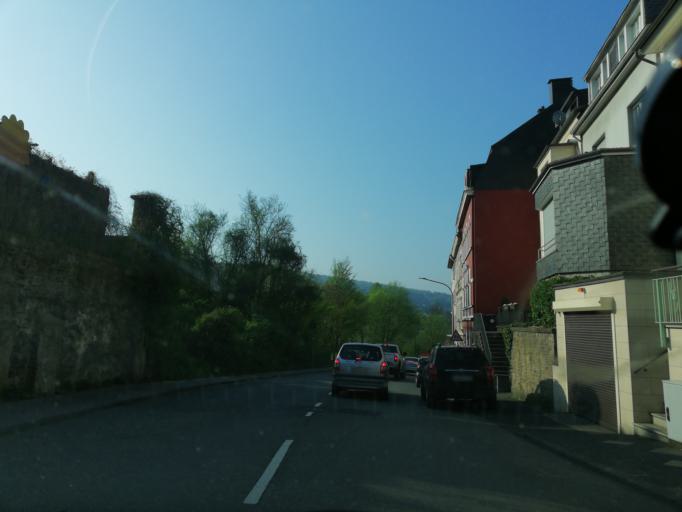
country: DE
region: North Rhine-Westphalia
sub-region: Regierungsbezirk Arnsberg
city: Schwelm
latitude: 51.2724
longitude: 7.2374
